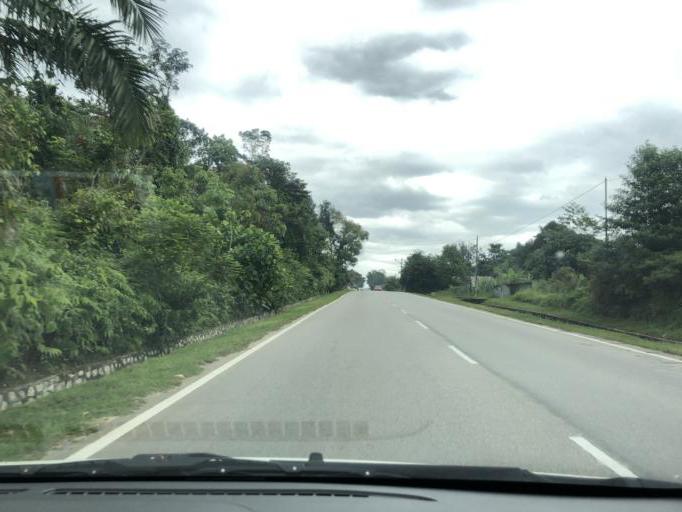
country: MY
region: Putrajaya
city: Putrajaya
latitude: 2.9276
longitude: 101.7472
